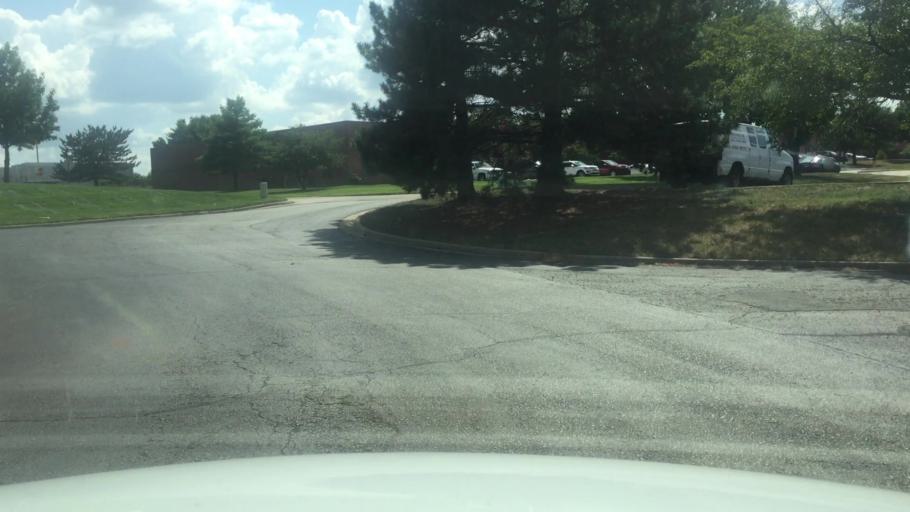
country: US
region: Kansas
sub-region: Johnson County
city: Lenexa
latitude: 38.9541
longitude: -94.7532
